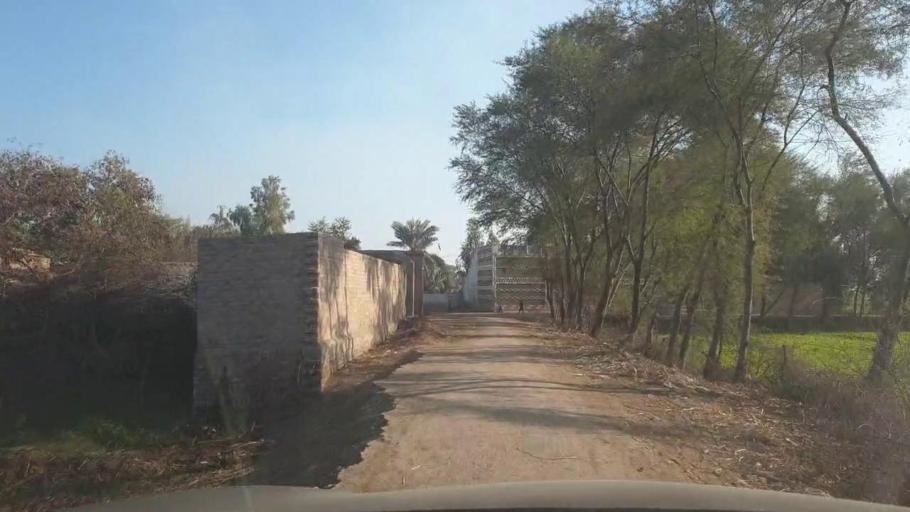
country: PK
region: Sindh
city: Ghotki
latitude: 28.0742
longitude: 69.3756
